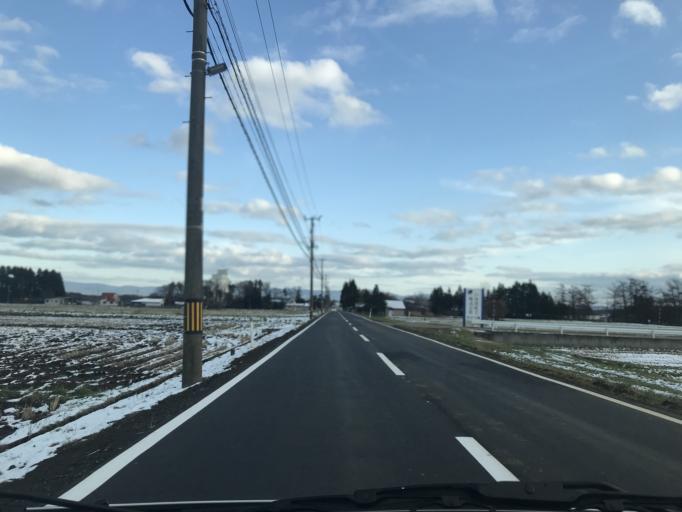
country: JP
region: Iwate
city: Kitakami
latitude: 39.2069
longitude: 141.0436
